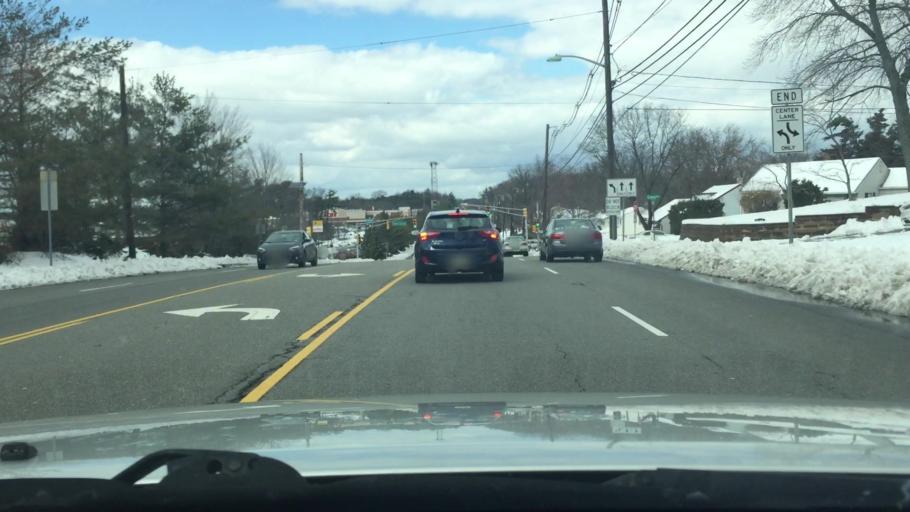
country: US
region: New Jersey
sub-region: Middlesex County
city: East Brunswick
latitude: 40.4408
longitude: -74.4232
